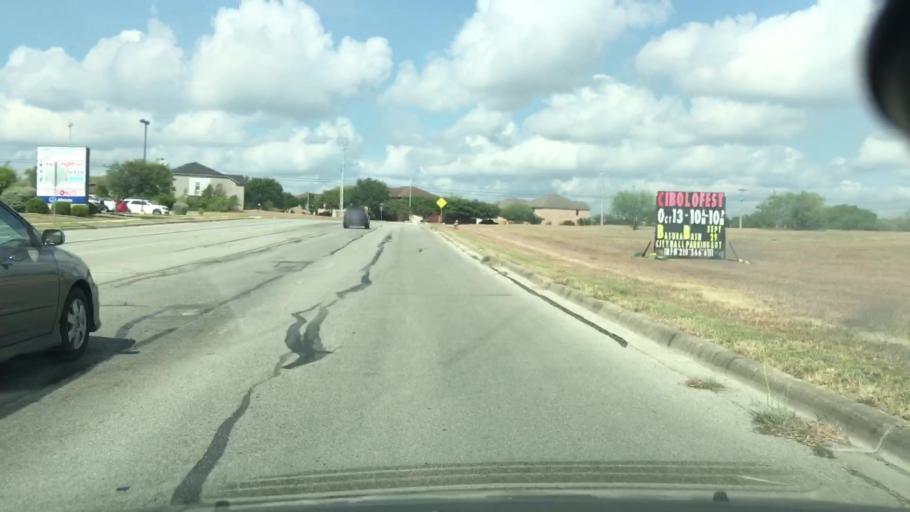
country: US
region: Texas
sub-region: Guadalupe County
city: Northcliff
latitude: 29.5949
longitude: -98.2530
